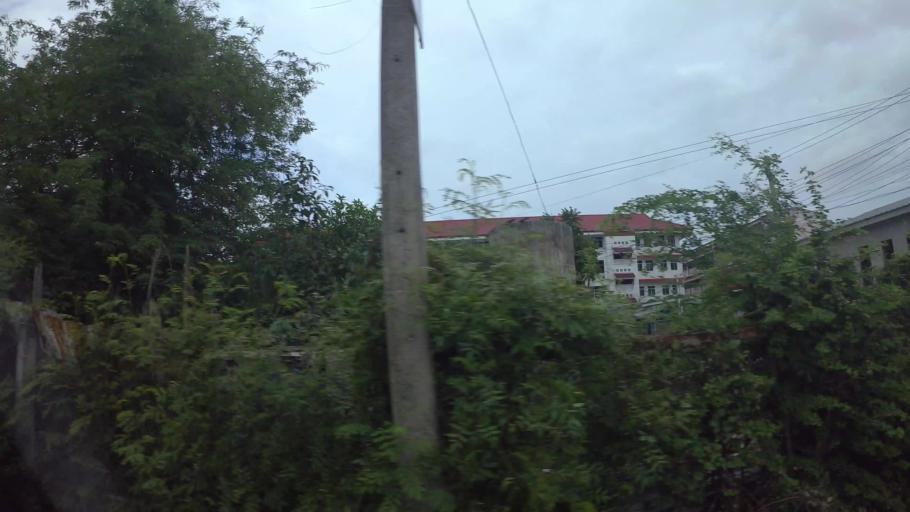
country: TH
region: Rayong
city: Rayong
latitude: 12.6822
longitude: 101.2717
